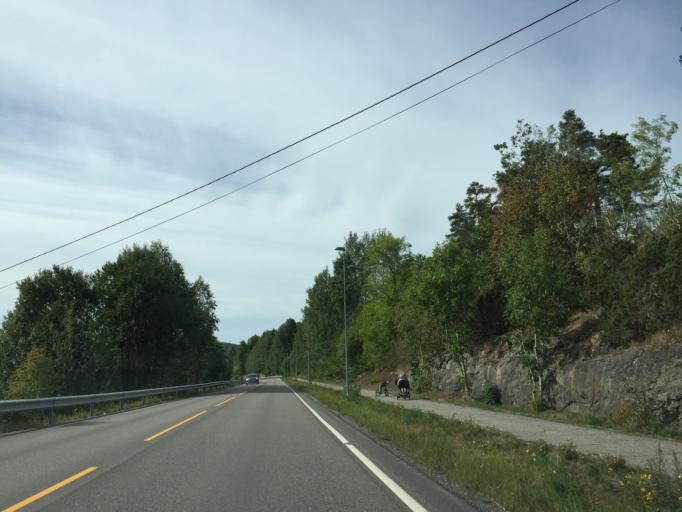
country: NO
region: Ostfold
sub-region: Moss
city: Moss
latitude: 59.5189
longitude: 10.6954
